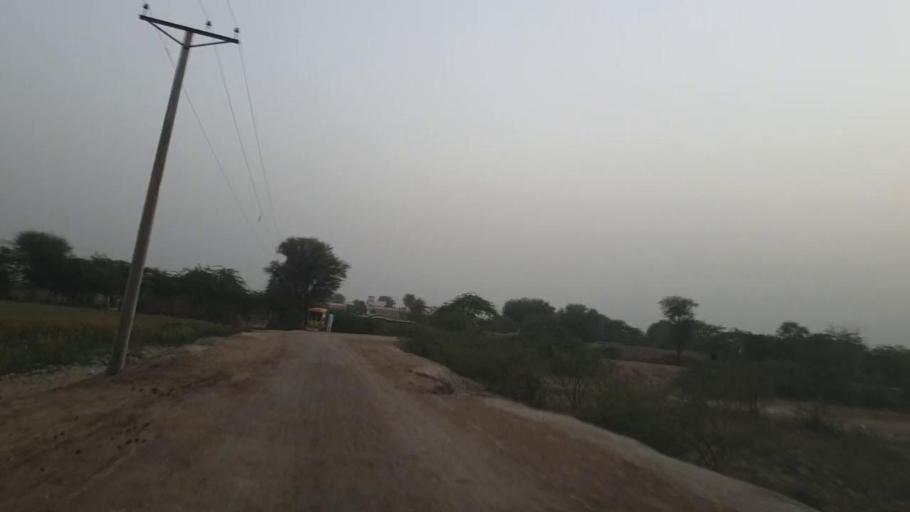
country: PK
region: Sindh
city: Kunri
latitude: 25.1083
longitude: 69.5681
